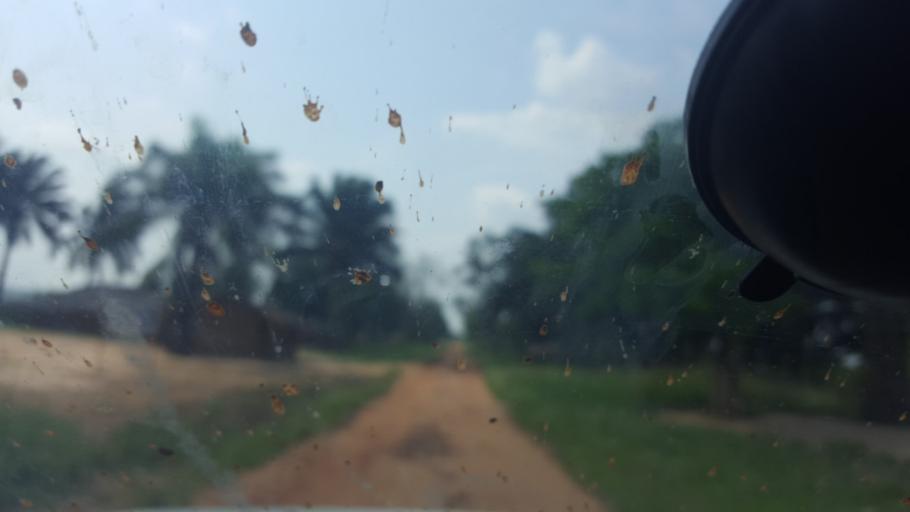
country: CD
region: Bandundu
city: Bandundu
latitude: -3.7517
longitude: 17.0389
